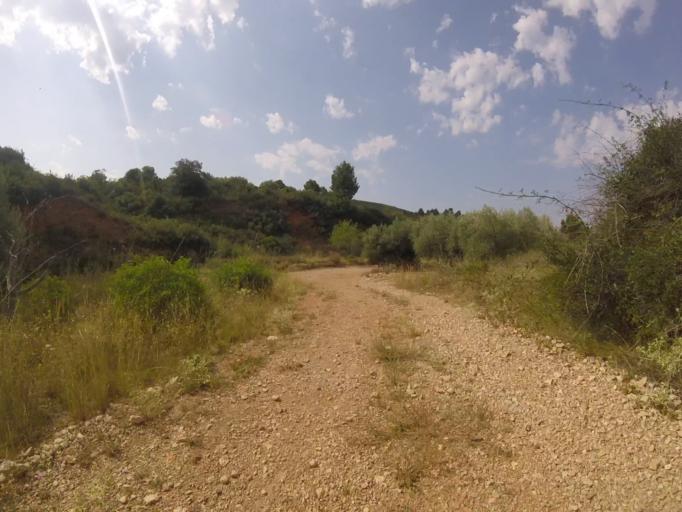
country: ES
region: Valencia
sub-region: Provincia de Castello
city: Alcala de Xivert
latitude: 40.3357
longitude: 0.1981
